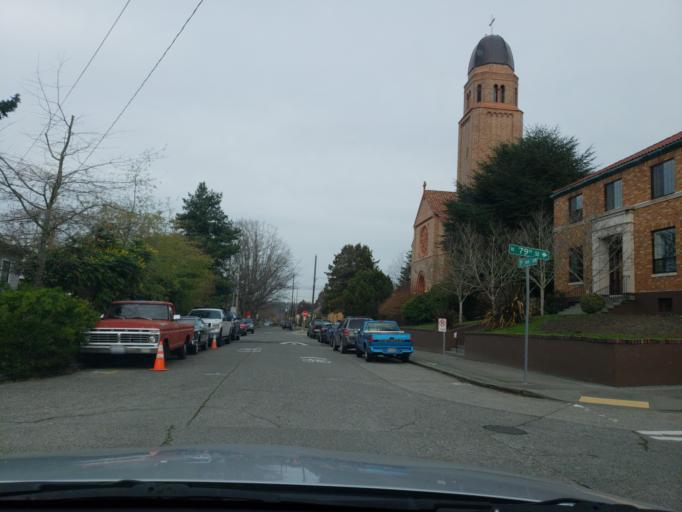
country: US
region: Washington
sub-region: King County
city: Shoreline
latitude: 47.6862
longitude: -122.3580
